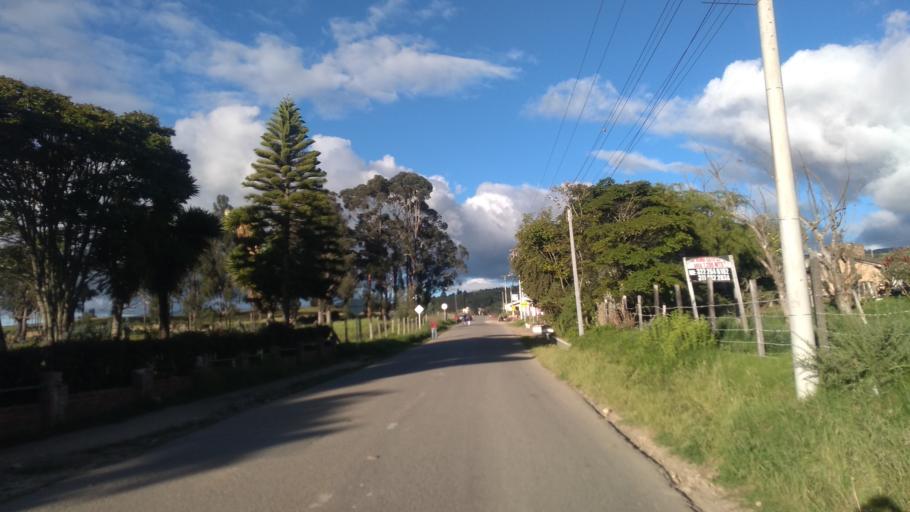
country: CO
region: Boyaca
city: Toca
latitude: 5.5675
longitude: -73.1919
